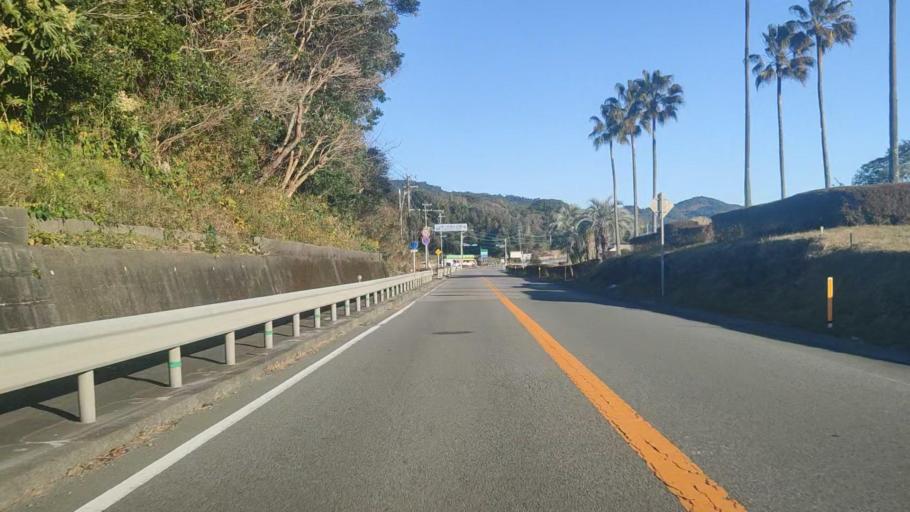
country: JP
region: Miyazaki
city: Nobeoka
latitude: 32.3549
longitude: 131.6211
